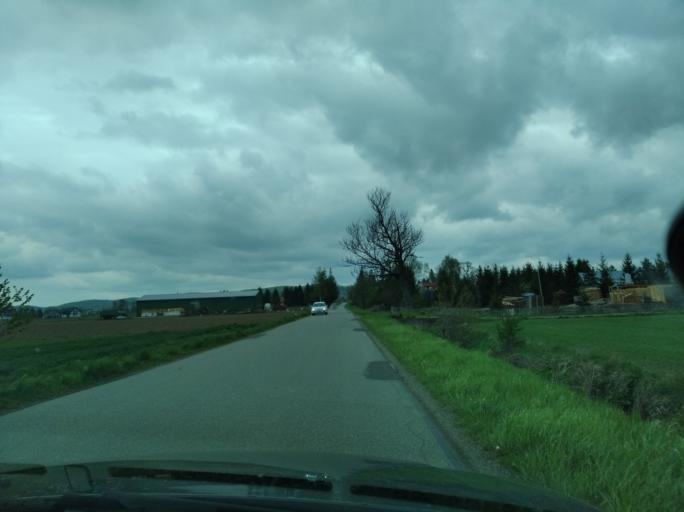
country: PL
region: Subcarpathian Voivodeship
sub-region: Powiat sanocki
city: Dlugie
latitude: 49.5905
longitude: 22.0481
